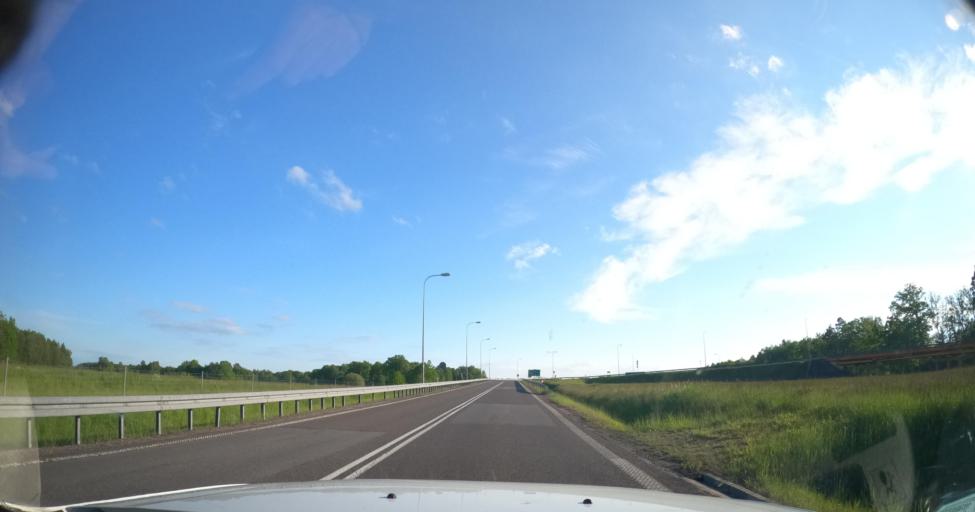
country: PL
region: Warmian-Masurian Voivodeship
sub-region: Powiat braniewski
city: Braniewo
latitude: 54.2883
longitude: 19.7927
